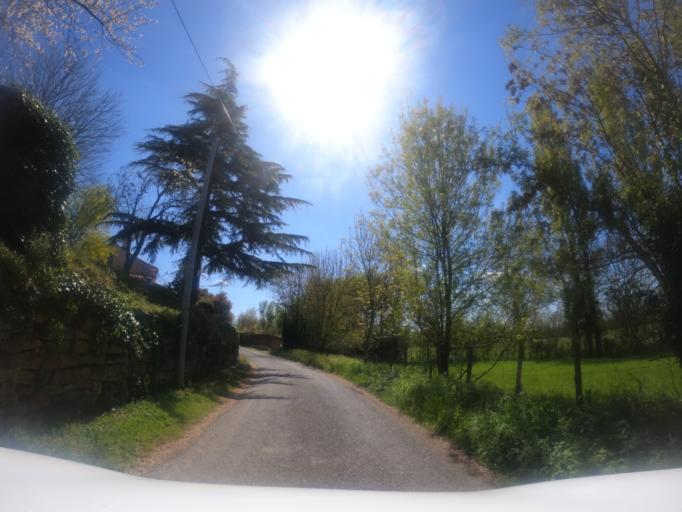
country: FR
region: Pays de la Loire
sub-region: Departement de la Vendee
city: Fontenay-le-Comte
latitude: 46.4350
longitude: -0.8746
